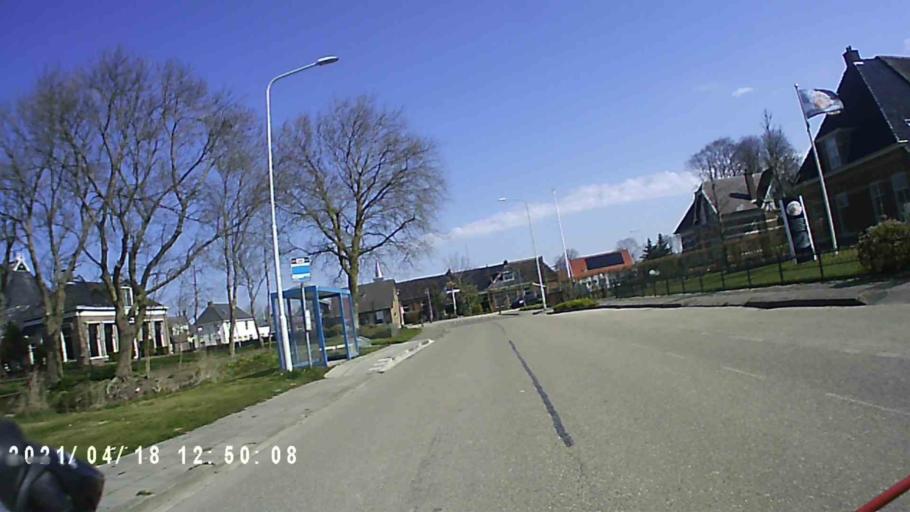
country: NL
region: Friesland
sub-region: Gemeente Dongeradeel
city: Anjum
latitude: 53.3770
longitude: 6.0548
